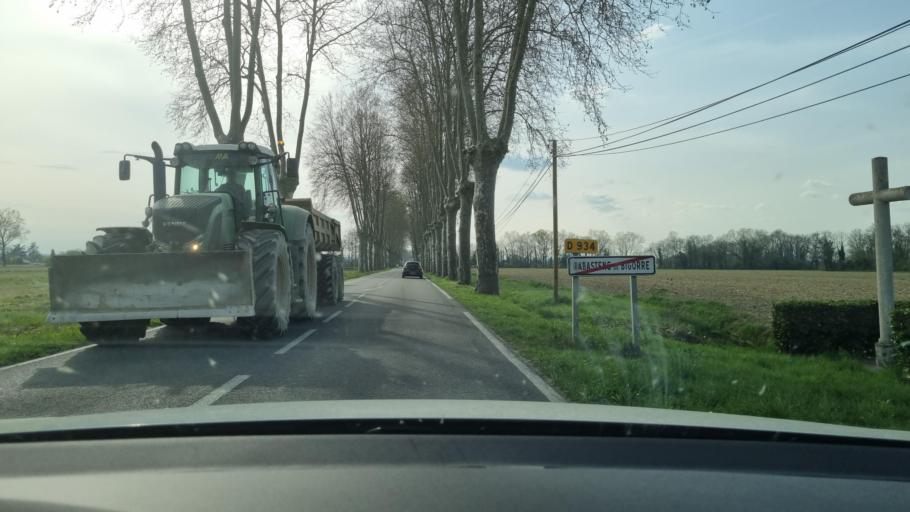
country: FR
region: Midi-Pyrenees
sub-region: Departement des Hautes-Pyrenees
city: Rabastens-de-Bigorre
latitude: 43.3874
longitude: 0.1394
